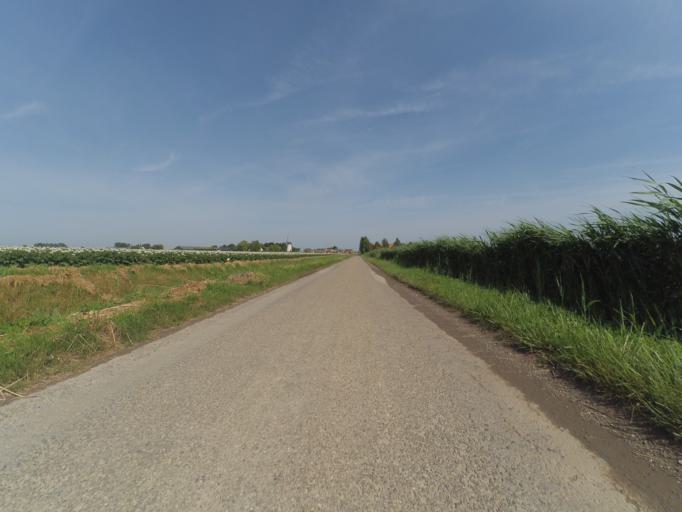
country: NL
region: North Brabant
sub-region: Gemeente Steenbergen
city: Nieuw-Vossemeer
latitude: 51.6001
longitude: 4.2494
